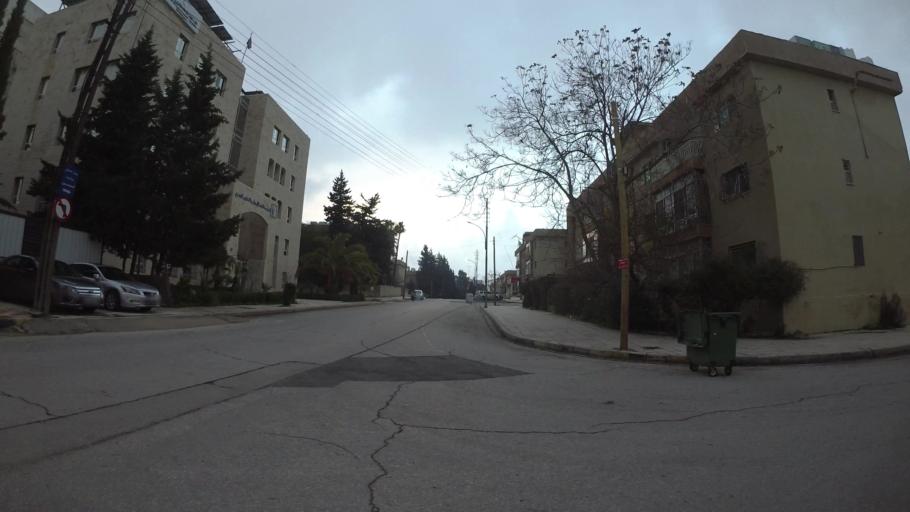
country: JO
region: Amman
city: Al Jubayhah
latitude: 31.9701
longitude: 35.8820
